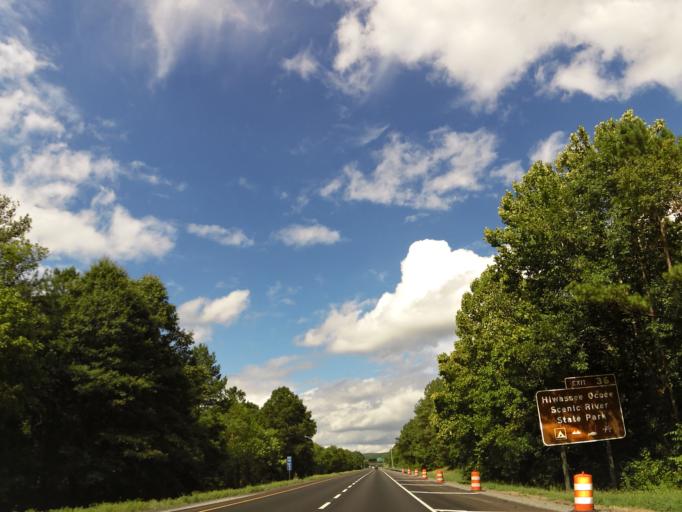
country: US
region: Tennessee
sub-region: Bradley County
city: Hopewell
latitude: 35.3268
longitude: -84.7720
